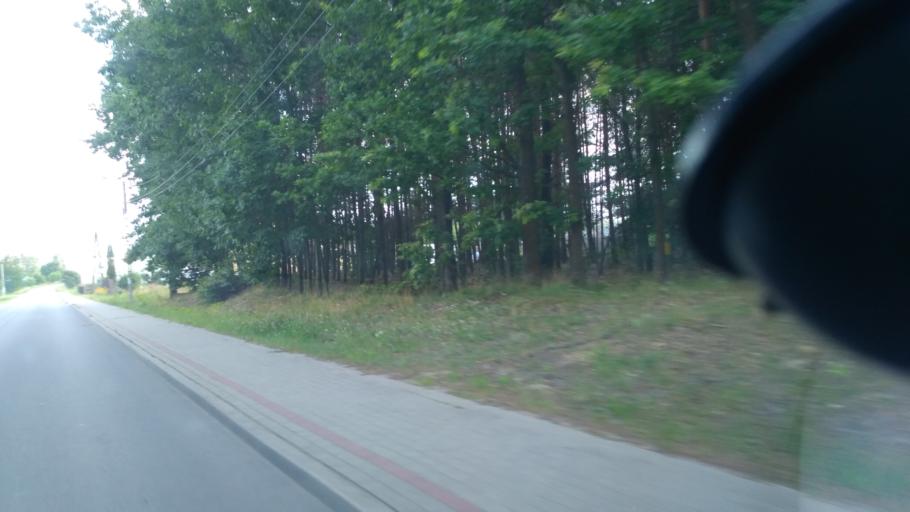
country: PL
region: Subcarpathian Voivodeship
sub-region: Powiat rzeszowski
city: Wysoka Glogowska
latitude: 50.1292
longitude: 22.0246
